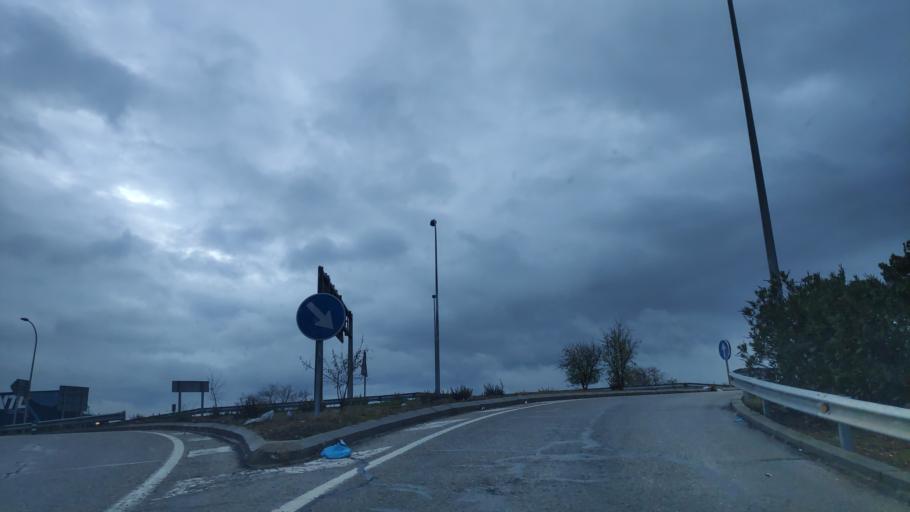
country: ES
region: Madrid
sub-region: Provincia de Madrid
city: Coslada
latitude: 40.4409
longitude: -3.5740
